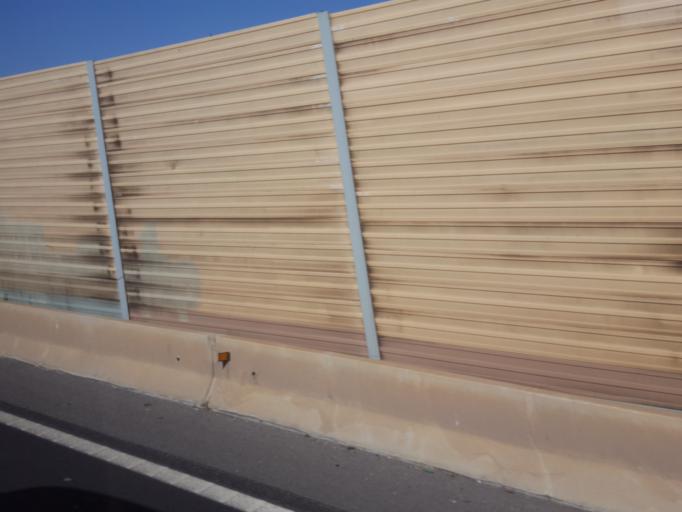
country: ES
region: Murcia
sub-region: Murcia
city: Murcia
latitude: 38.0021
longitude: -1.1614
